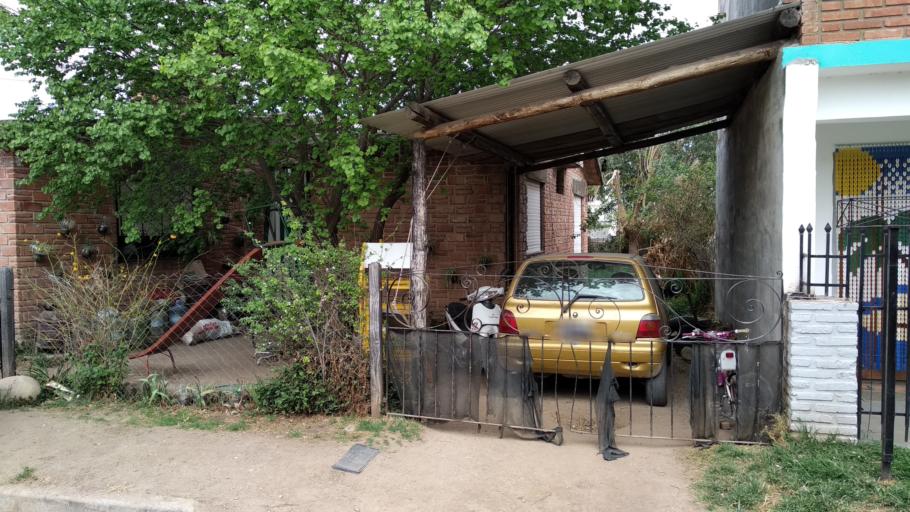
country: AR
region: Cordoba
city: Mina Clavero
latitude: -31.7291
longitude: -65.0105
